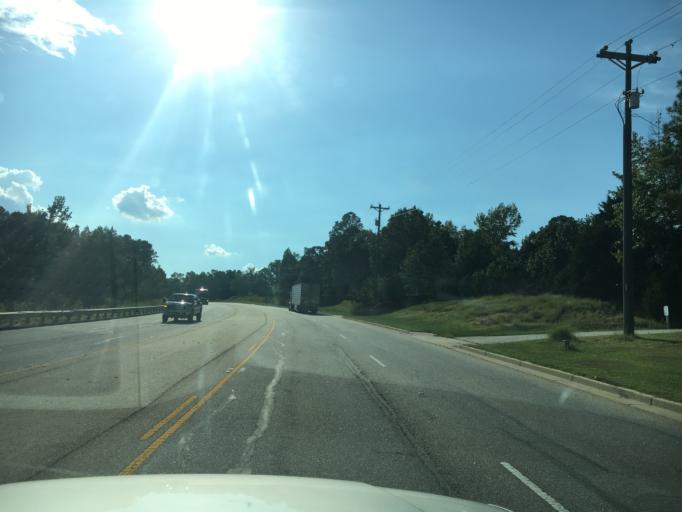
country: US
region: South Carolina
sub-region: Greenwood County
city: Ninety Six
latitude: 34.2901
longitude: -82.0350
